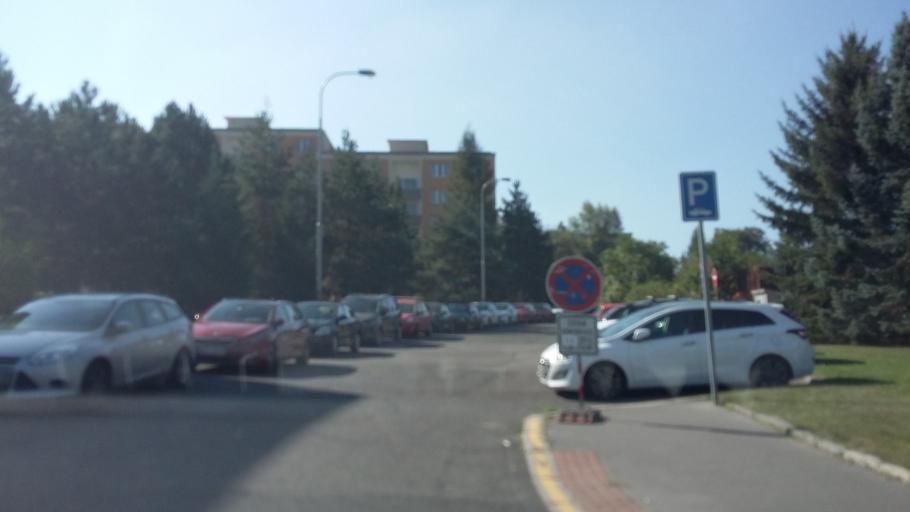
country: CZ
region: Praha
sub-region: Praha 9
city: Vysocany
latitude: 50.0590
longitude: 14.5182
